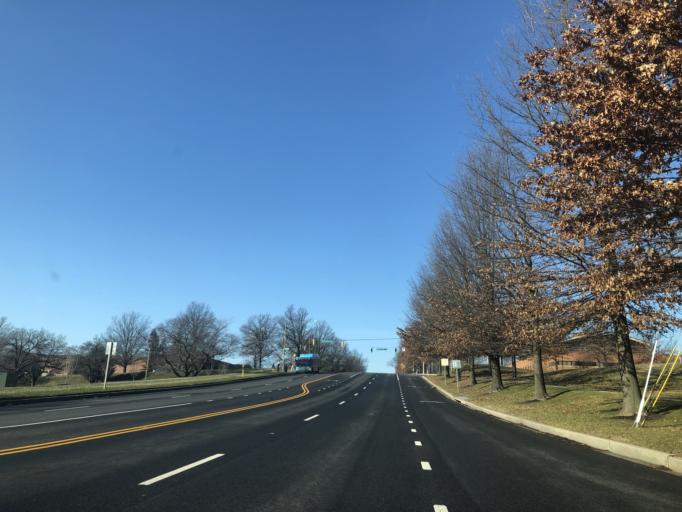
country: US
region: Maryland
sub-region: Montgomery County
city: Gaithersburg
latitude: 39.1474
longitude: -77.2314
